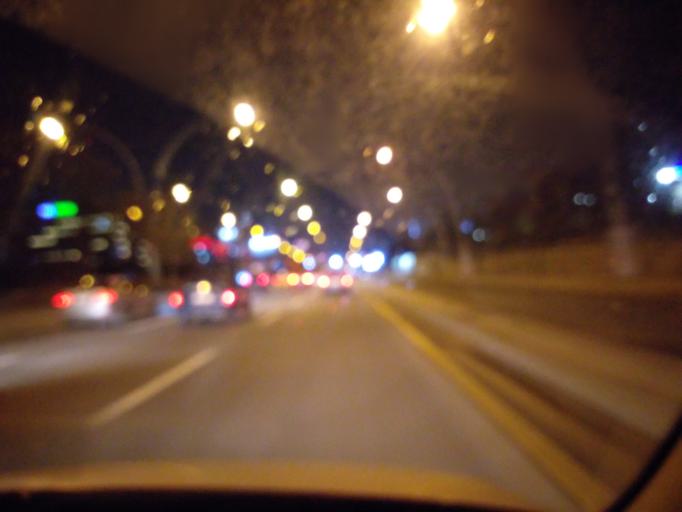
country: TR
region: Ankara
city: Batikent
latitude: 39.9067
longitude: 32.7409
